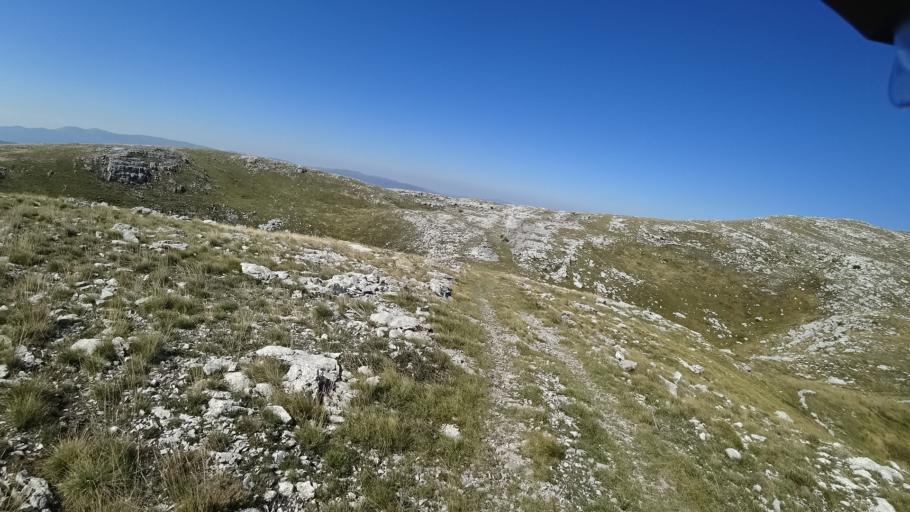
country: HR
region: Splitsko-Dalmatinska
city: Hrvace
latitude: 43.9164
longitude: 16.6056
